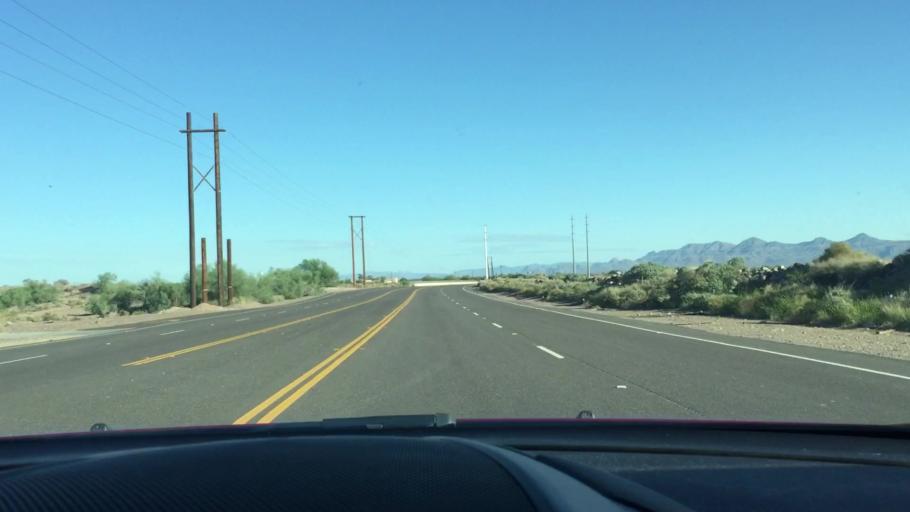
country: US
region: Arizona
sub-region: Maricopa County
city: Mesa
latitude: 33.4500
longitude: -111.8570
